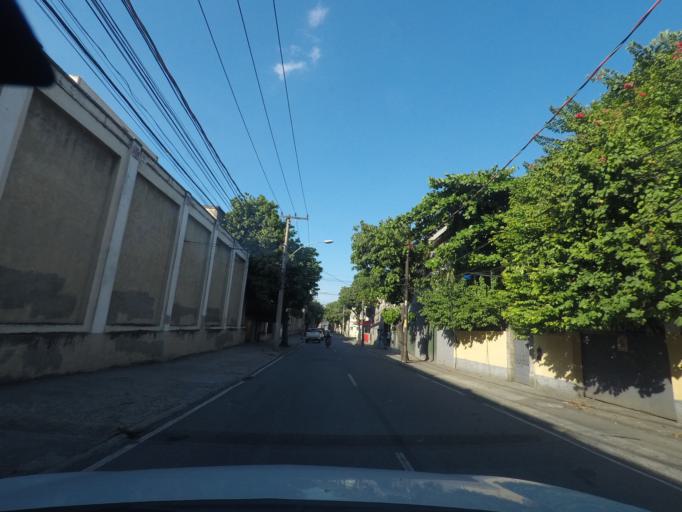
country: BR
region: Rio de Janeiro
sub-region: Rio De Janeiro
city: Rio de Janeiro
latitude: -22.8927
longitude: -43.2275
